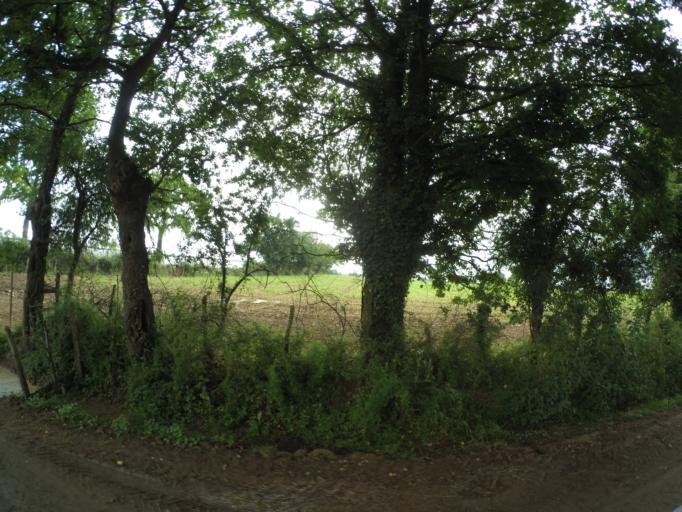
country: FR
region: Pays de la Loire
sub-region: Departement de la Vendee
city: Nesmy
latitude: 46.6084
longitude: -1.3935
